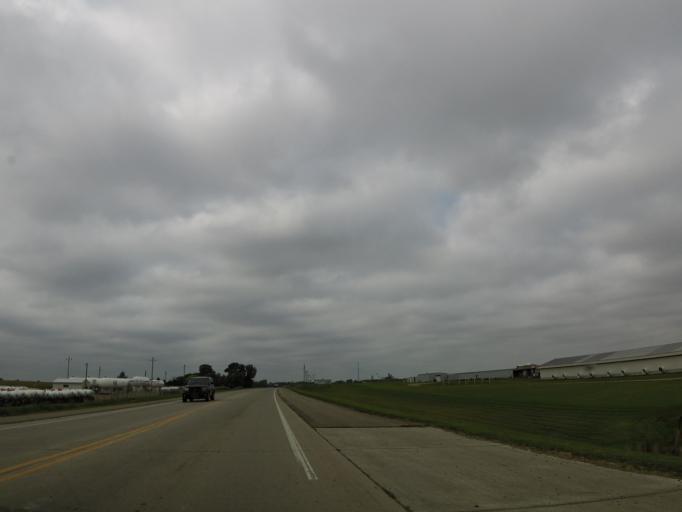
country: US
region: Minnesota
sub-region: Renville County
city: Renville
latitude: 44.7892
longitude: -95.1835
